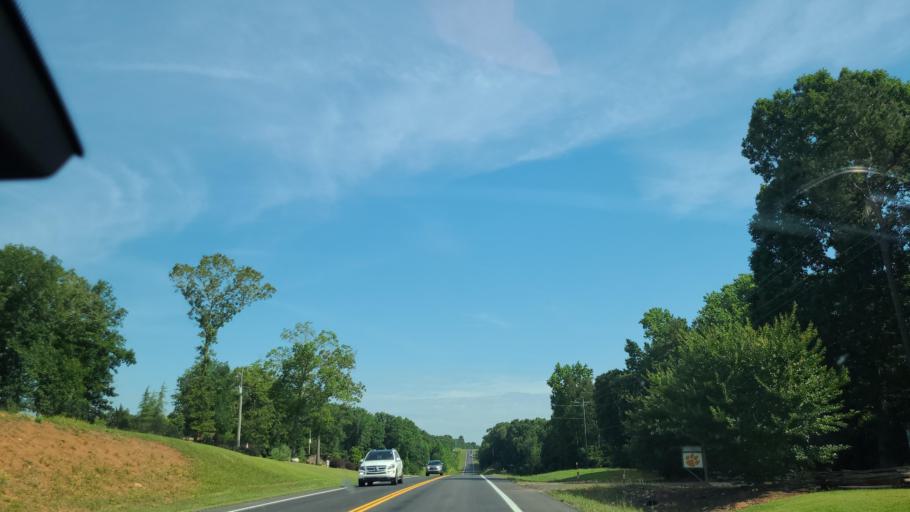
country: US
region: Georgia
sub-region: Franklin County
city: Gumlog
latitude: 34.5165
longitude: -83.0468
